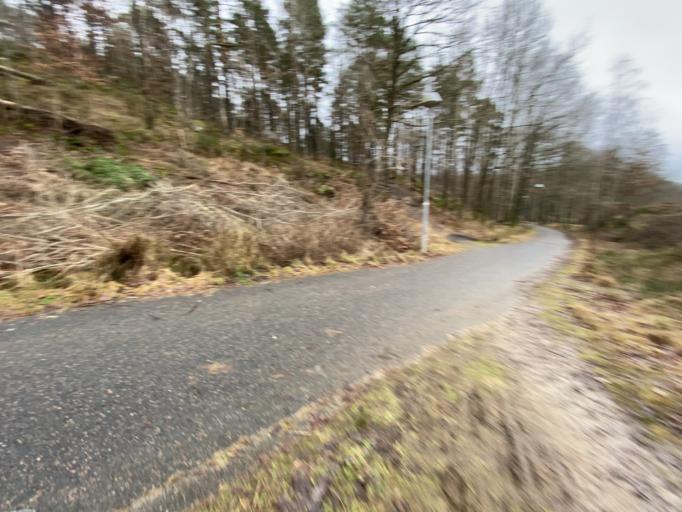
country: SE
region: Vaestra Goetaland
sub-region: Molndal
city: Moelndal
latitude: 57.7086
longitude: 12.0395
